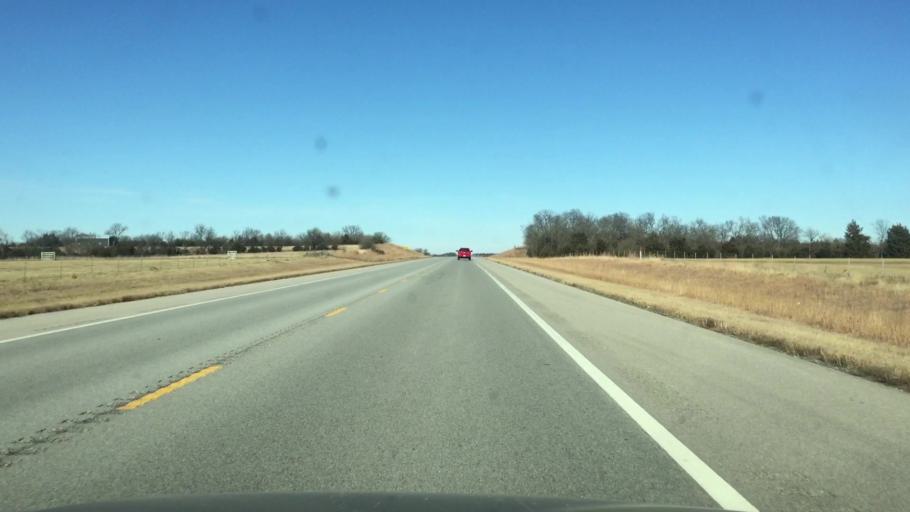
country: US
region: Kansas
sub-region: Allen County
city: Iola
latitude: 37.9682
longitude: -95.3813
